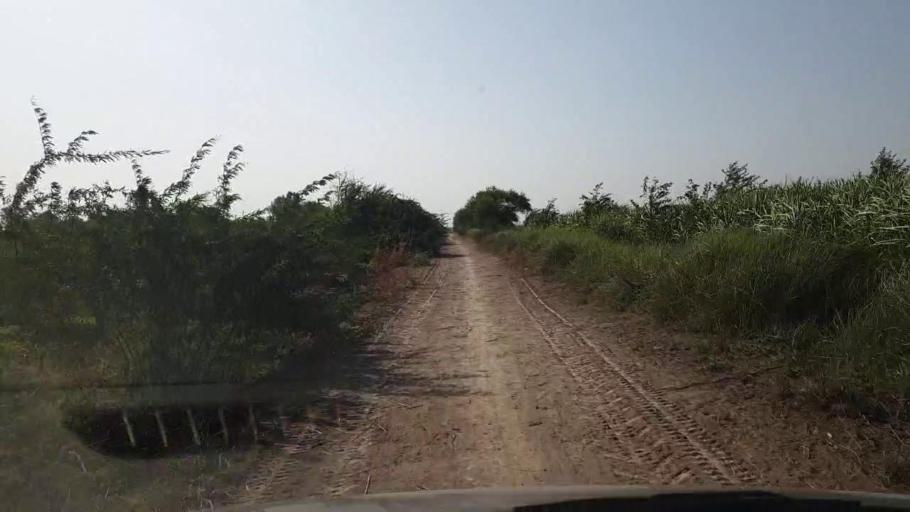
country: PK
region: Sindh
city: Kadhan
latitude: 24.5995
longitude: 69.0750
